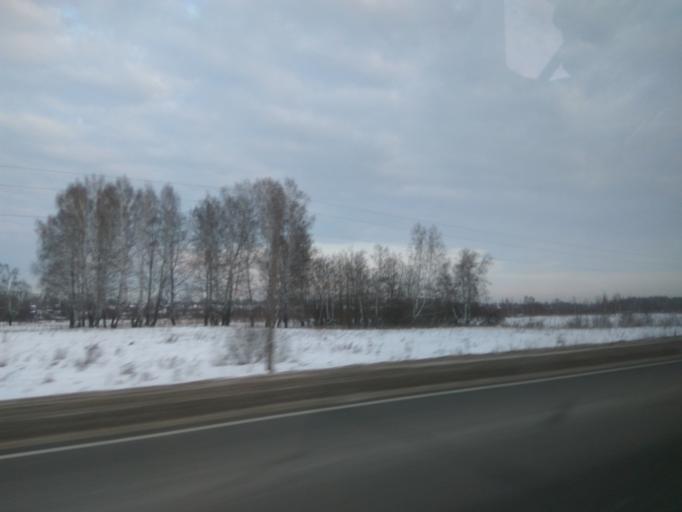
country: RU
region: Novosibirsk
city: Bolotnoye
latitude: 55.6479
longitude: 84.3687
